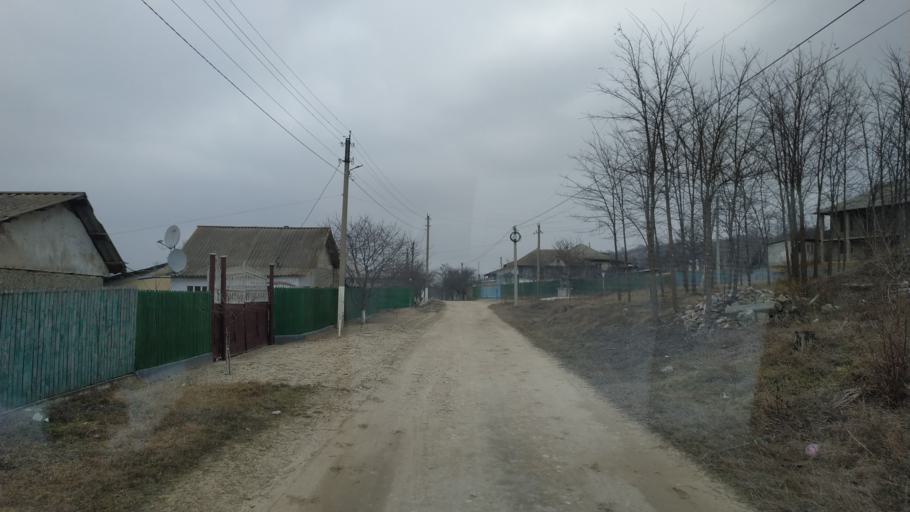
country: MD
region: Hincesti
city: Hincesti
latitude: 46.8886
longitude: 28.4050
